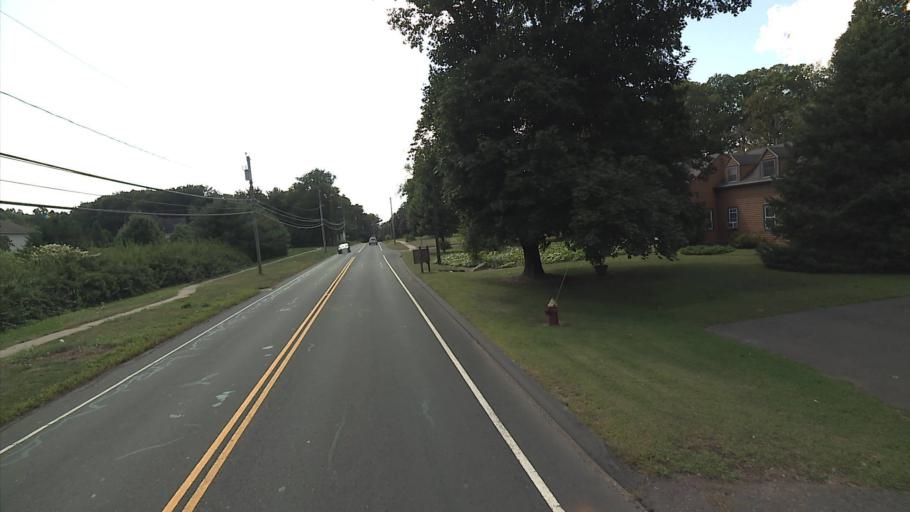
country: US
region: Connecticut
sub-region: Hartford County
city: Newington
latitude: 41.6496
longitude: -72.7104
